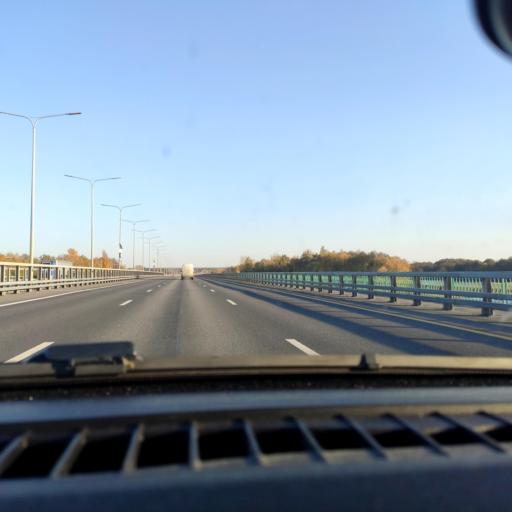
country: RU
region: Voronezj
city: Somovo
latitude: 51.7932
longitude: 39.2665
